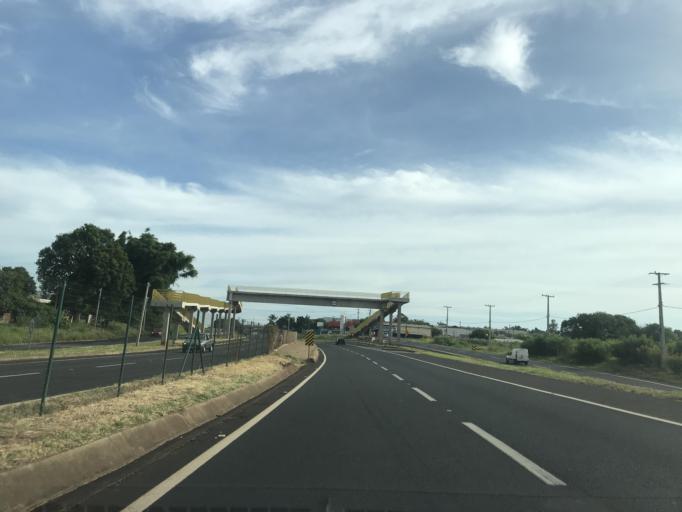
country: BR
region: Parana
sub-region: Mandaguacu
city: Mandaguacu
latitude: -23.3474
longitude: -52.0902
